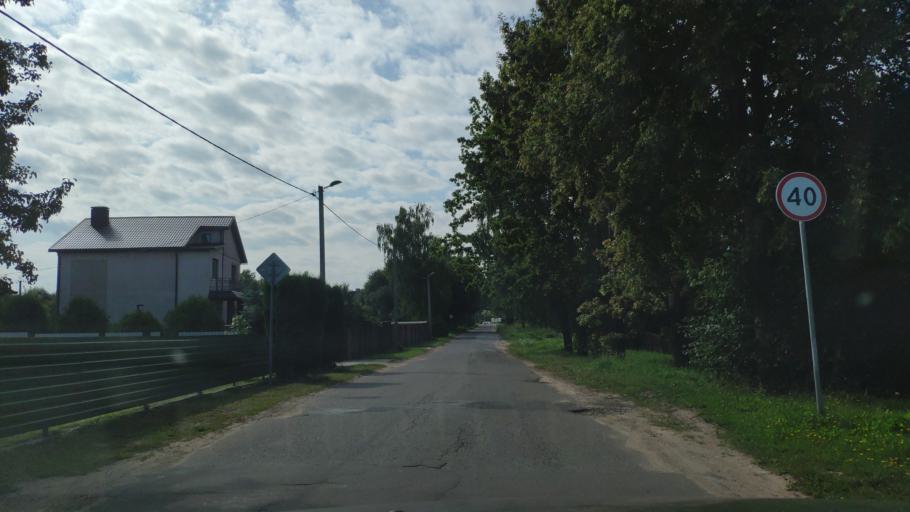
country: BY
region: Minsk
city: Zaslawye
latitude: 53.9932
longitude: 27.2840
